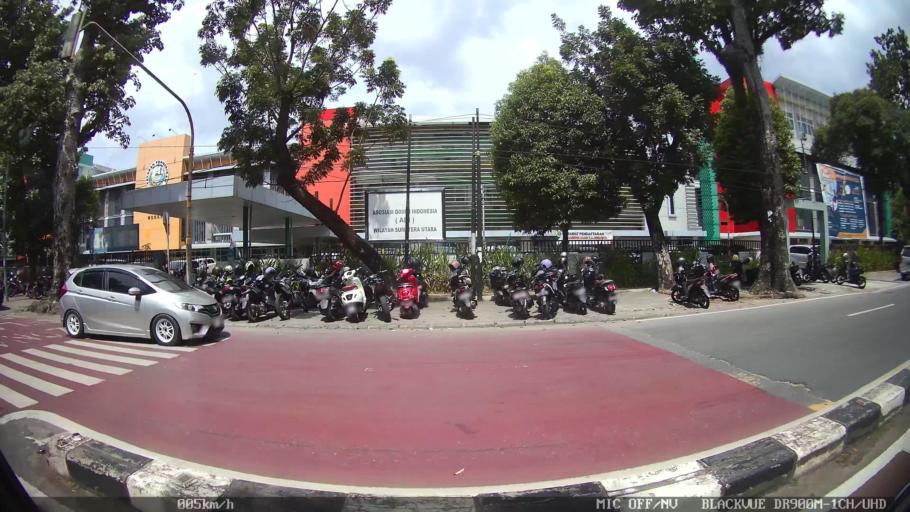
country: ID
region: North Sumatra
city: Medan
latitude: 3.5760
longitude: 98.6774
